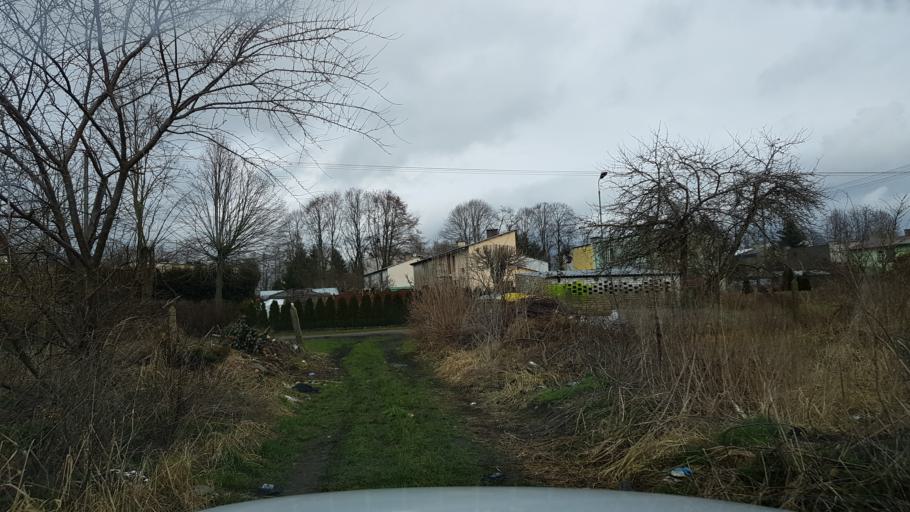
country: PL
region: West Pomeranian Voivodeship
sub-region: Powiat swidwinski
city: Swidwin
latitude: 53.7747
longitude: 15.8548
